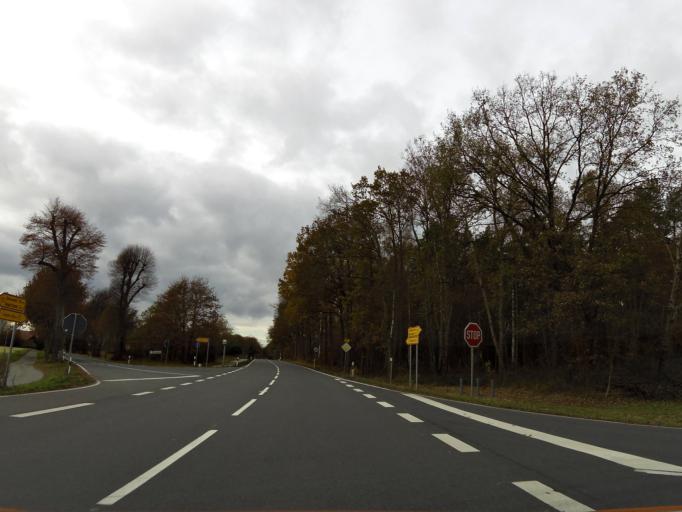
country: DE
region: Lower Saxony
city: Schnega
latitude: 52.9065
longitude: 10.9191
